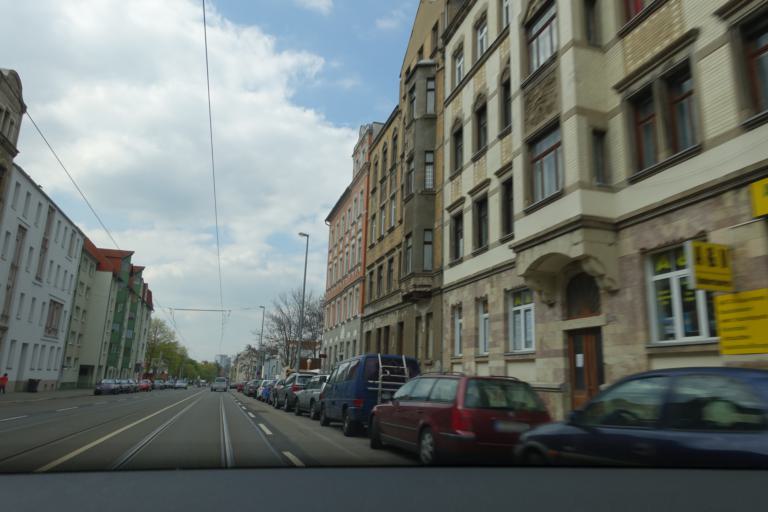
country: DE
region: Saxony
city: Chemnitz
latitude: 50.8191
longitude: 12.9371
